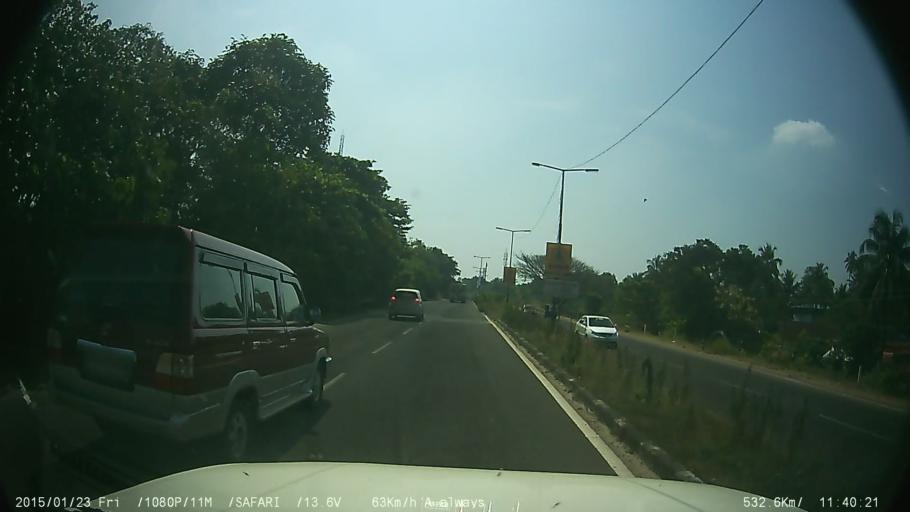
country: IN
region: Kerala
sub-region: Alappuzha
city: Kutiatodu
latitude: 9.7934
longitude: 76.3163
